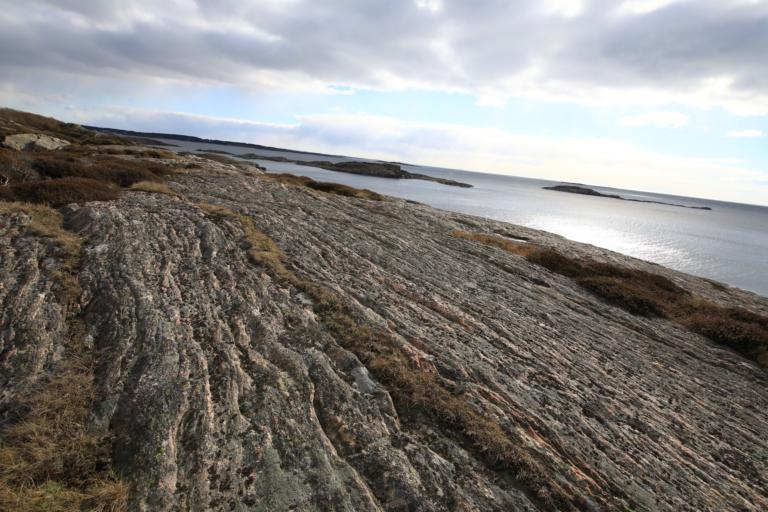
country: SE
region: Halland
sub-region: Kungsbacka Kommun
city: Frillesas
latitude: 57.2167
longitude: 12.1361
